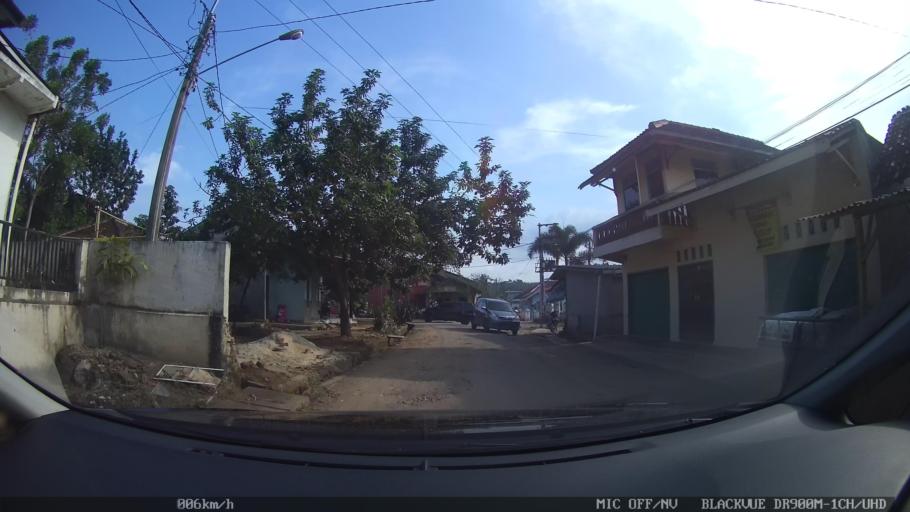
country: ID
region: Lampung
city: Kedaton
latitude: -5.3721
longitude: 105.2362
